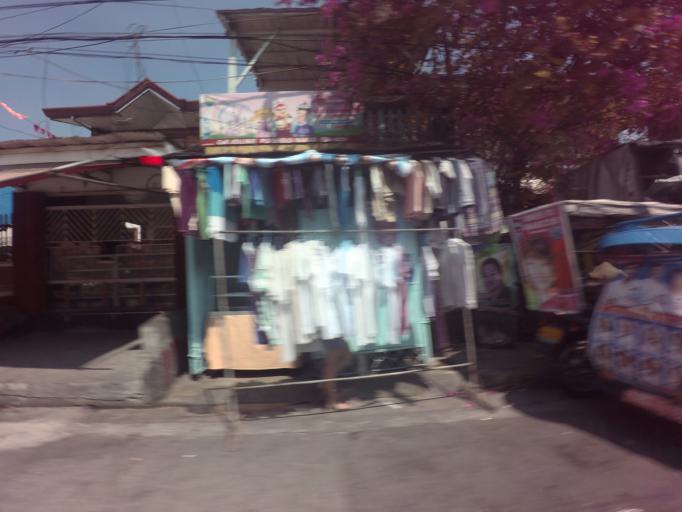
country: PH
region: Metro Manila
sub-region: Makati City
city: Makati City
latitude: 14.5721
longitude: 121.0118
